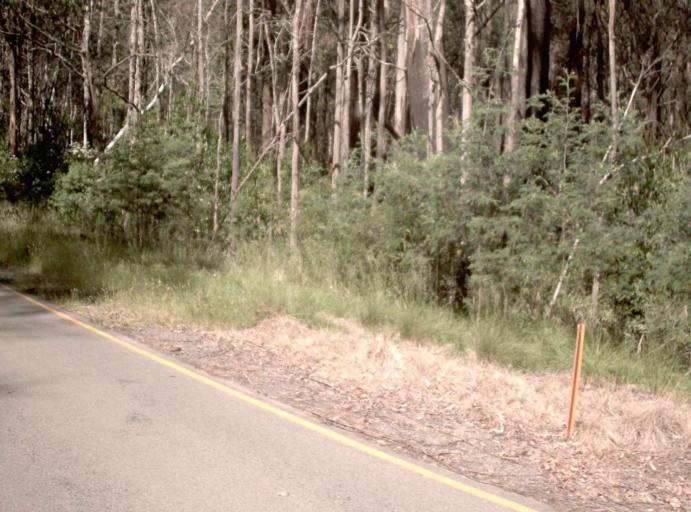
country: AU
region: Victoria
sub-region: Yarra Ranges
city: Millgrove
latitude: -37.5616
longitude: 145.8930
